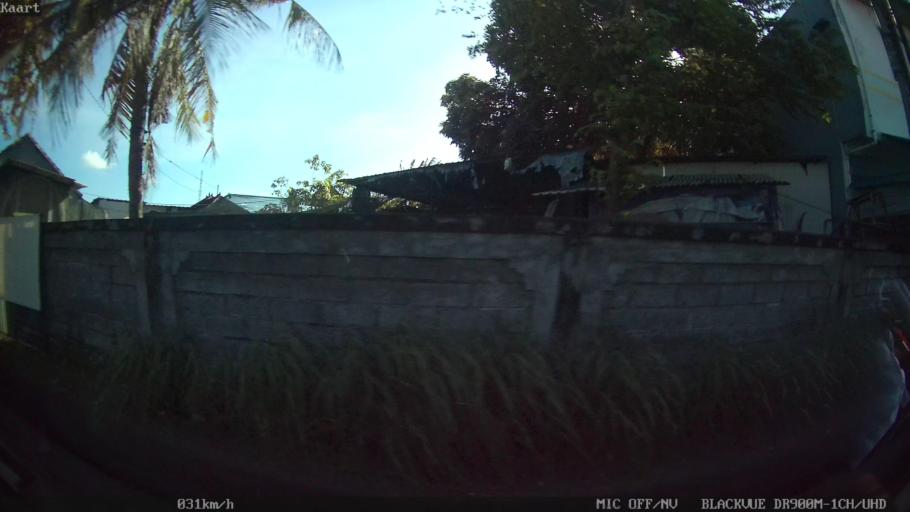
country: ID
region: Bali
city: Banjar Gunungpande
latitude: -8.6428
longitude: 115.1706
